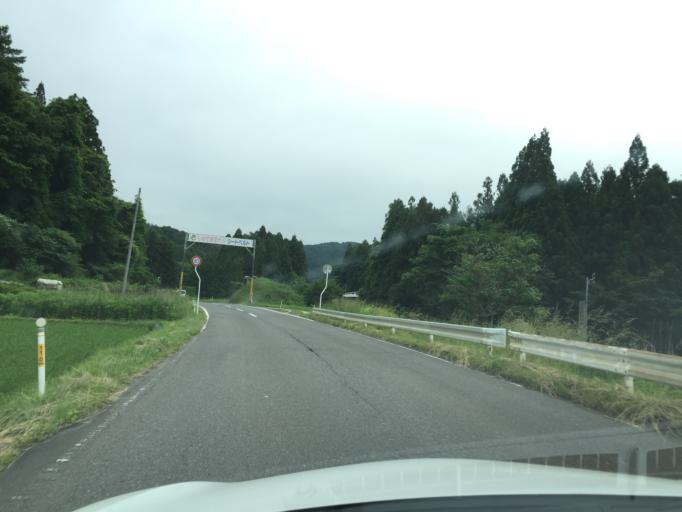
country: JP
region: Fukushima
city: Funehikimachi-funehiki
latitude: 37.3654
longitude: 140.6384
